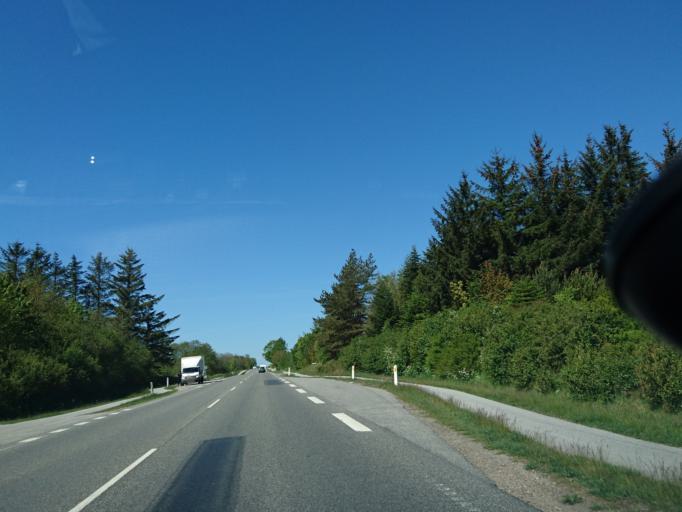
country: DK
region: North Denmark
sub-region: Hjorring Kommune
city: Tars
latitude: 57.4554
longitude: 10.1085
